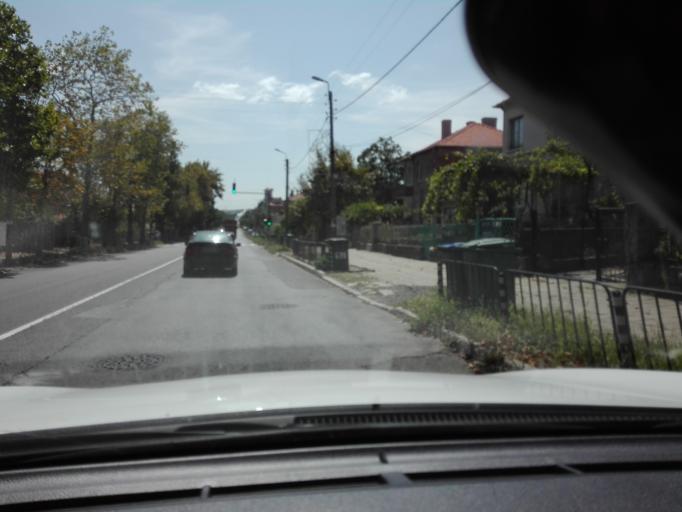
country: BG
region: Burgas
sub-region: Obshtina Kameno
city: Kameno
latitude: 42.6026
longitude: 27.3860
